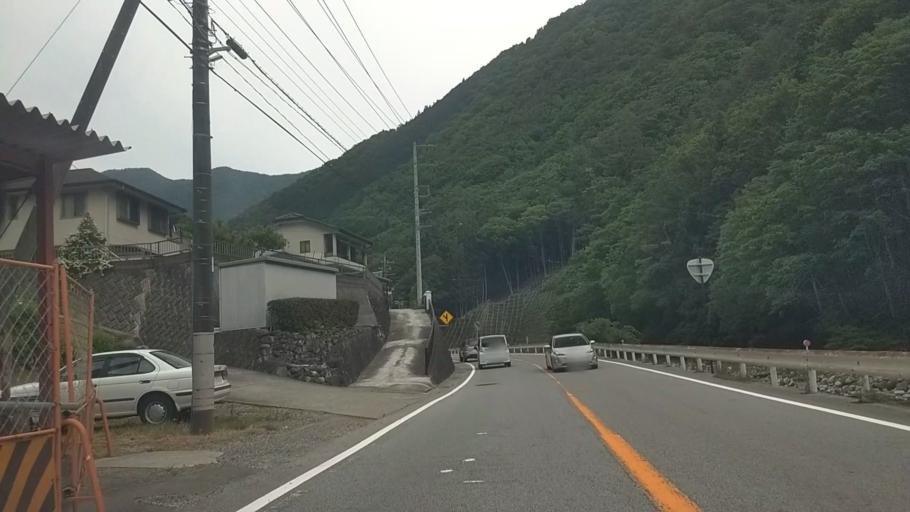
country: JP
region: Yamanashi
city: Fujikawaguchiko
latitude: 35.5319
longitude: 138.6071
